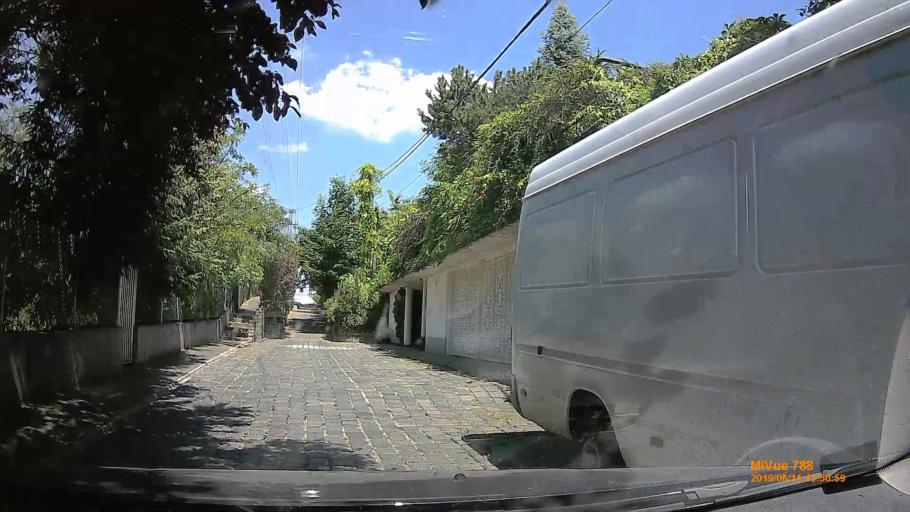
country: HU
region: Budapest
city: Budapest XXIII. keruelet
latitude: 47.3788
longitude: 19.1068
